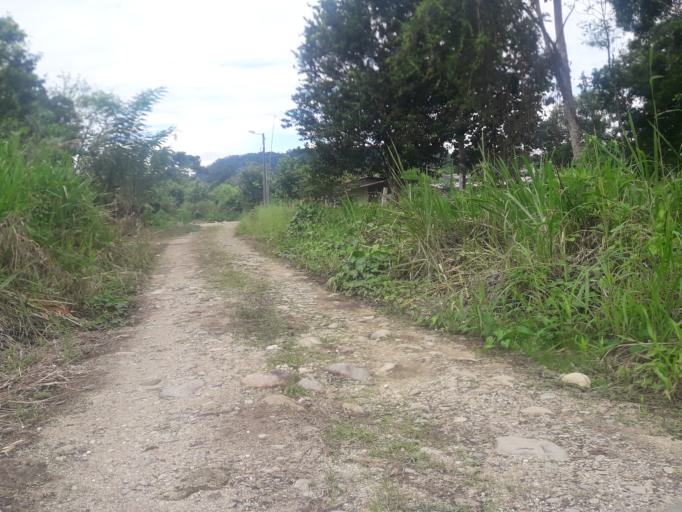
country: EC
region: Napo
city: Tena
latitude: -0.9746
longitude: -77.8467
